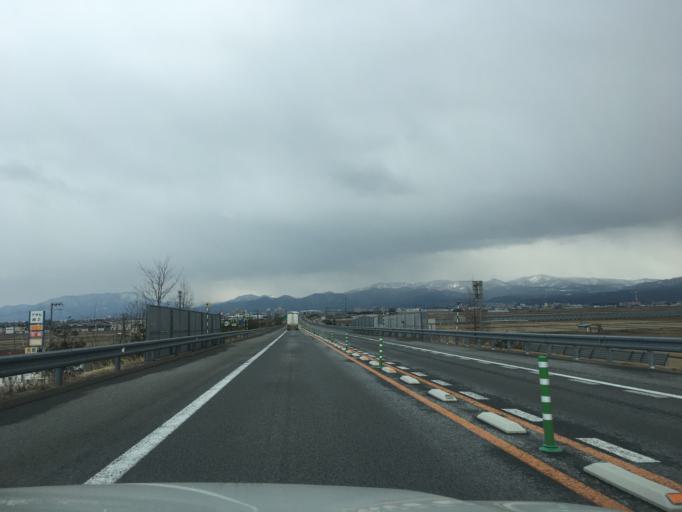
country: JP
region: Aomori
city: Aomori Shi
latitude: 40.7976
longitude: 140.7132
